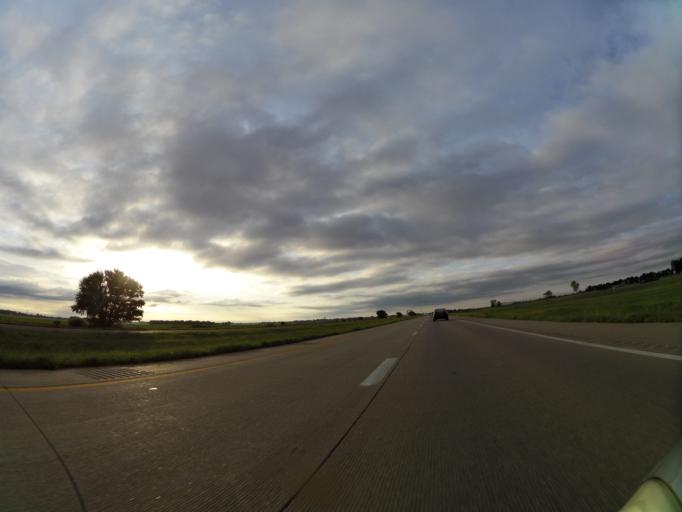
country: US
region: Kansas
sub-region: Reno County
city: Haven
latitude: 37.9098
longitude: -97.8087
